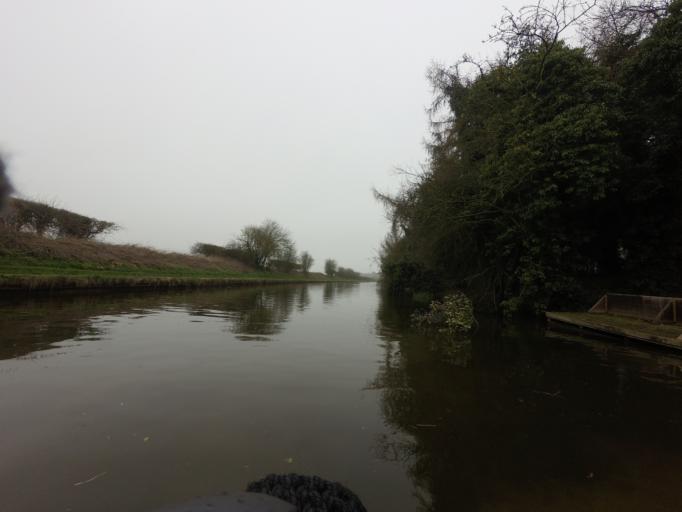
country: GB
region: England
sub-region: Hertfordshire
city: Tring
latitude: 51.7895
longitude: -0.6177
